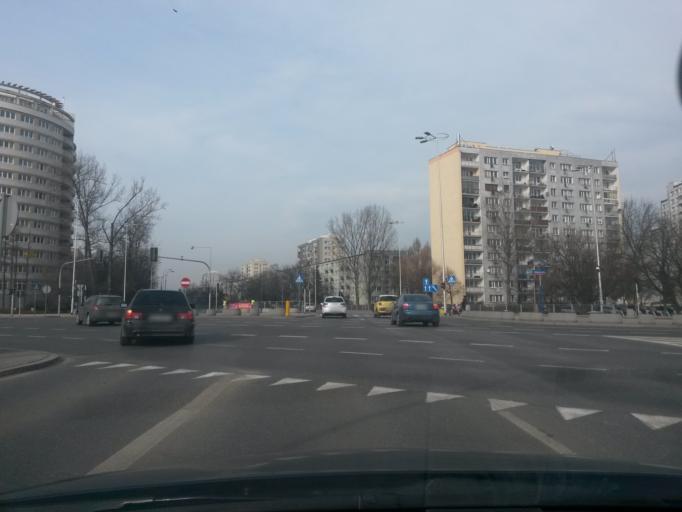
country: PL
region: Masovian Voivodeship
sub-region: Warszawa
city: Wilanow
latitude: 52.1695
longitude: 21.0683
